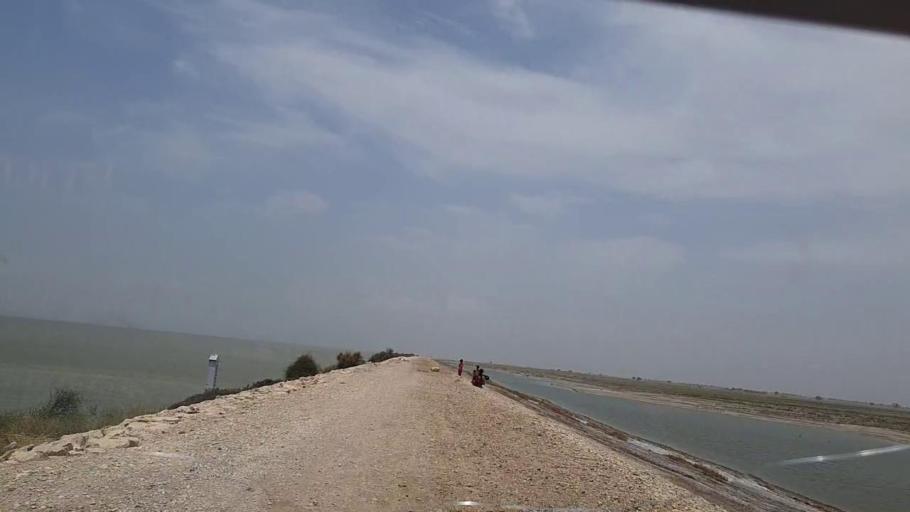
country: PK
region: Sindh
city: Sehwan
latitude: 26.4182
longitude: 67.7414
